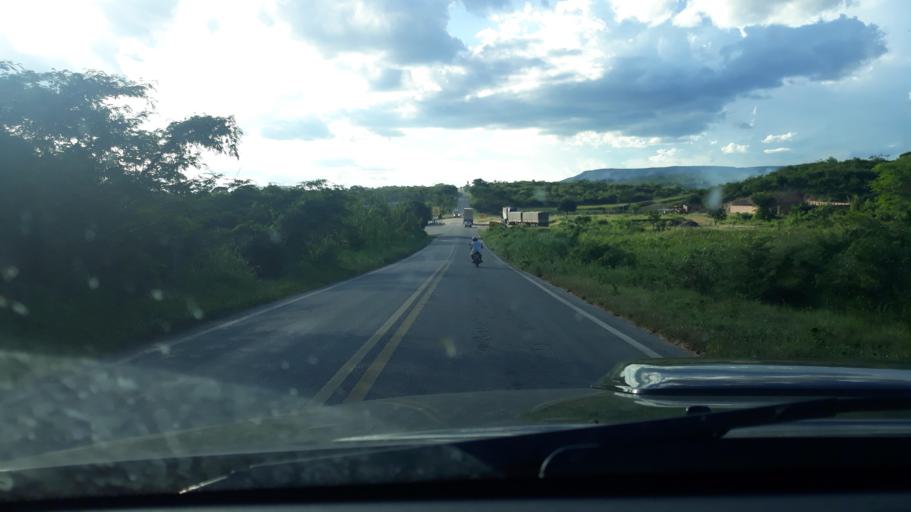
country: BR
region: Bahia
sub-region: Riacho De Santana
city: Riacho de Santana
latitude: -13.7654
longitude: -42.7257
